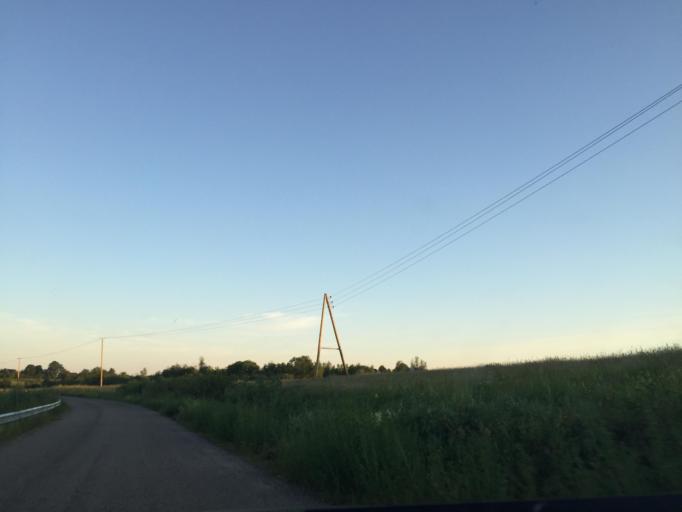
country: LV
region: Rezekne
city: Rezekne
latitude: 56.3705
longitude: 27.4085
